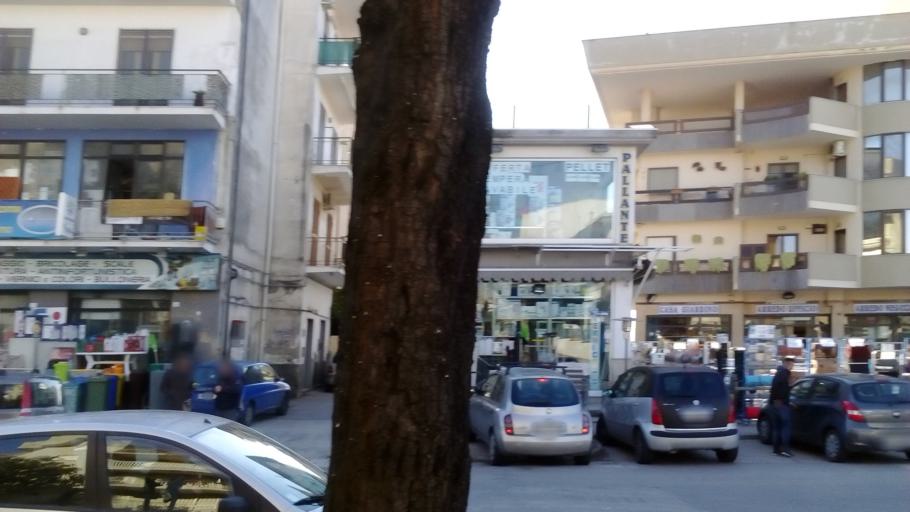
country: IT
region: Campania
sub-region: Provincia di Napoli
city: Casalnuovo di Napoli
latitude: 40.9015
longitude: 14.3462
